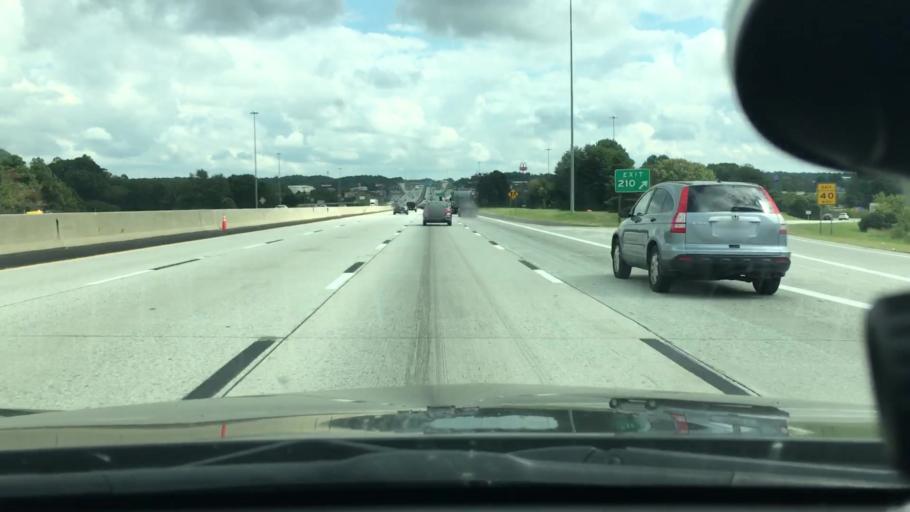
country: US
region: North Carolina
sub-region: Guilford County
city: Jamestown
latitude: 36.0819
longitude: -79.9640
